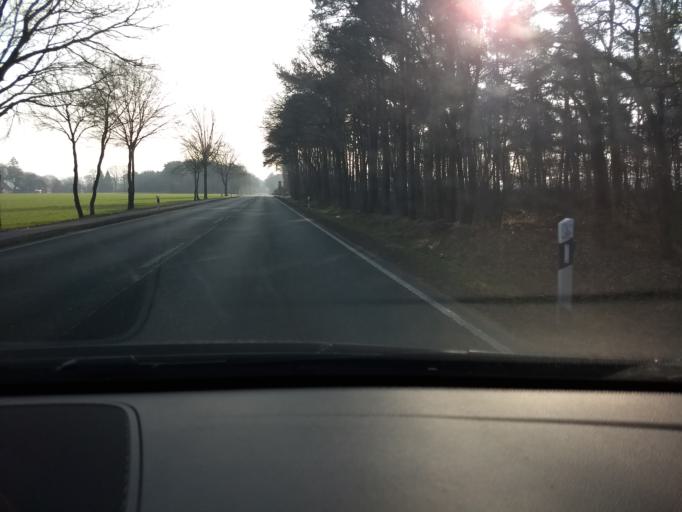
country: DE
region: North Rhine-Westphalia
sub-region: Regierungsbezirk Munster
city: Rhede
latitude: 51.8299
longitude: 6.7359
